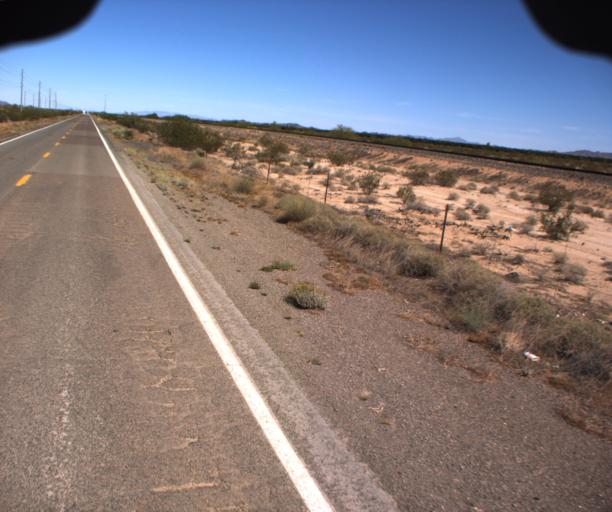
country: US
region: Arizona
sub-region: La Paz County
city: Salome
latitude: 33.8229
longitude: -113.8652
